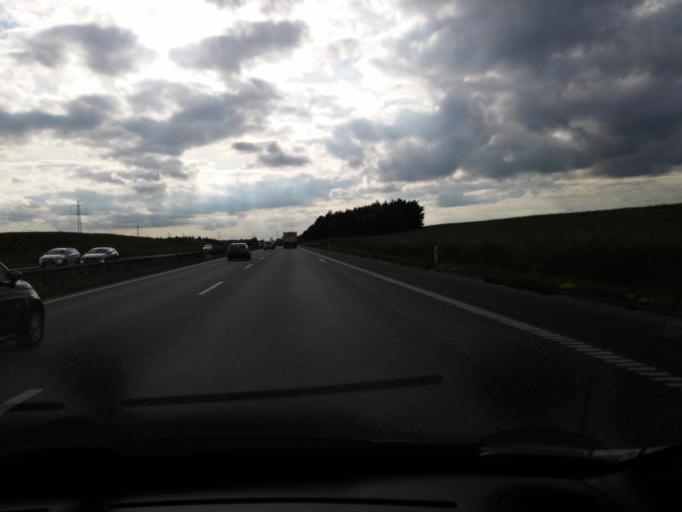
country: DK
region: Zealand
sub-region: Ringsted Kommune
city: Ringsted
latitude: 55.4566
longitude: 11.7794
